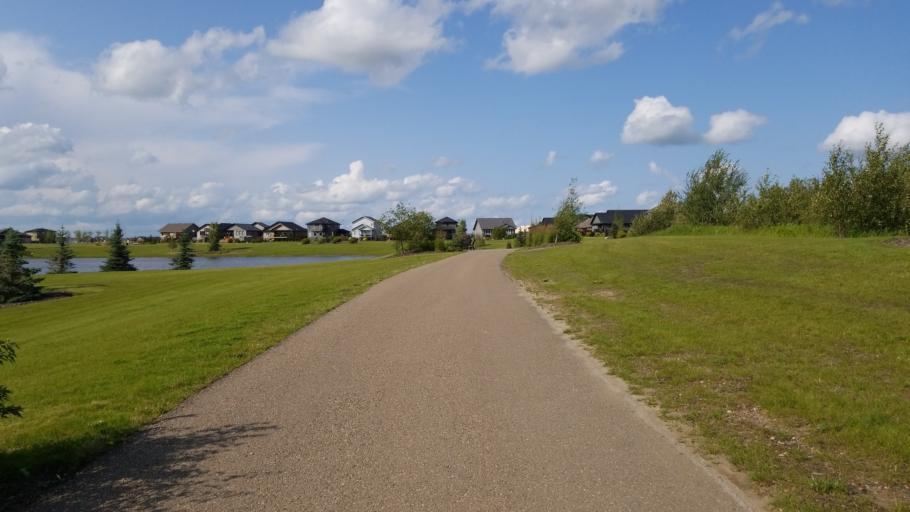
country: CA
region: Saskatchewan
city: Lloydminster
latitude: 53.2621
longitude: -110.0469
